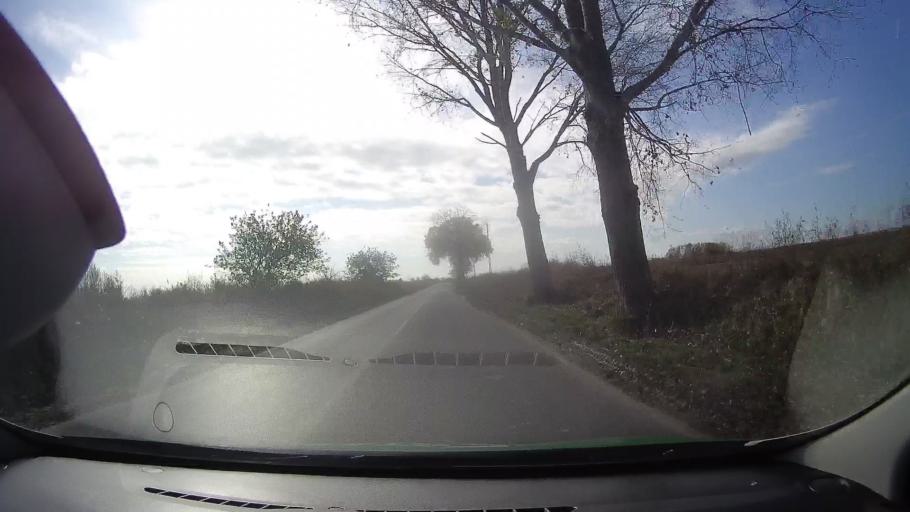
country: RO
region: Tulcea
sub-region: Comuna Valea Nucarilor
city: Agighiol
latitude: 44.9859
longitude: 28.8843
